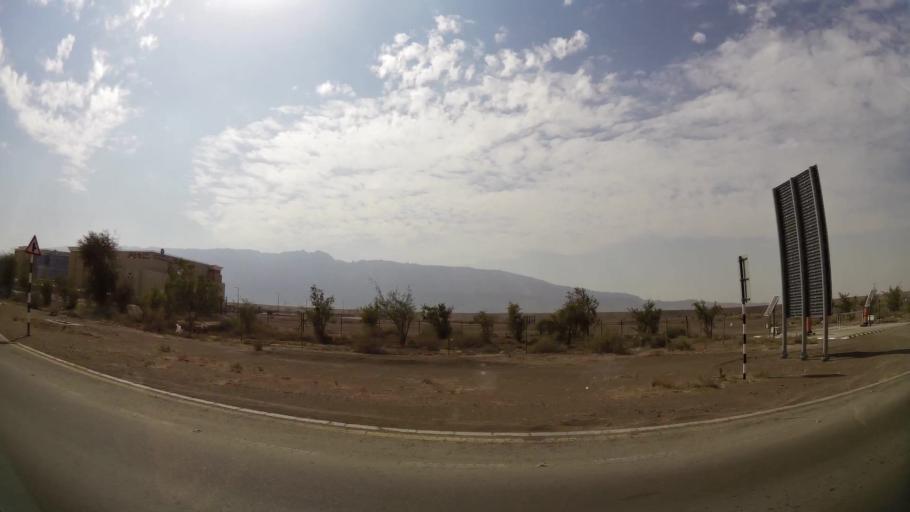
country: AE
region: Abu Dhabi
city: Al Ain
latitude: 24.0883
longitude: 55.8312
